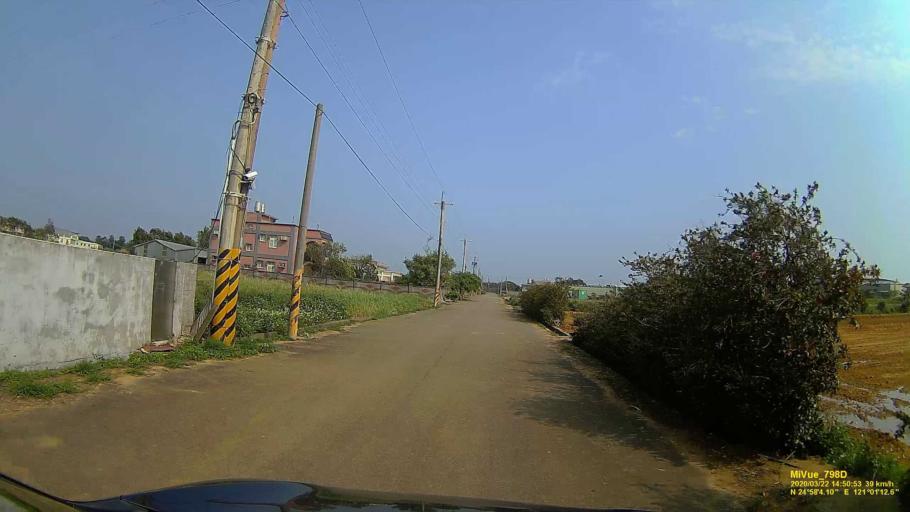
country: TW
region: Taiwan
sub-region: Hsinchu
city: Zhubei
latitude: 24.9678
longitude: 121.0204
